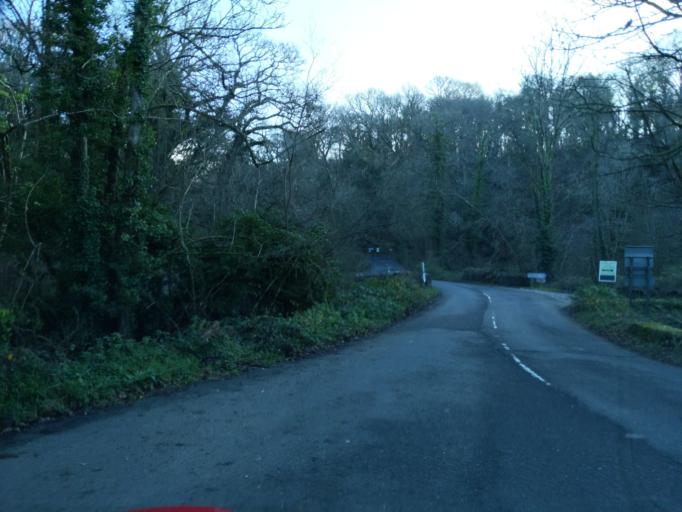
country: GB
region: England
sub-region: Cornwall
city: Pillaton
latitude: 50.4127
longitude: -4.3325
